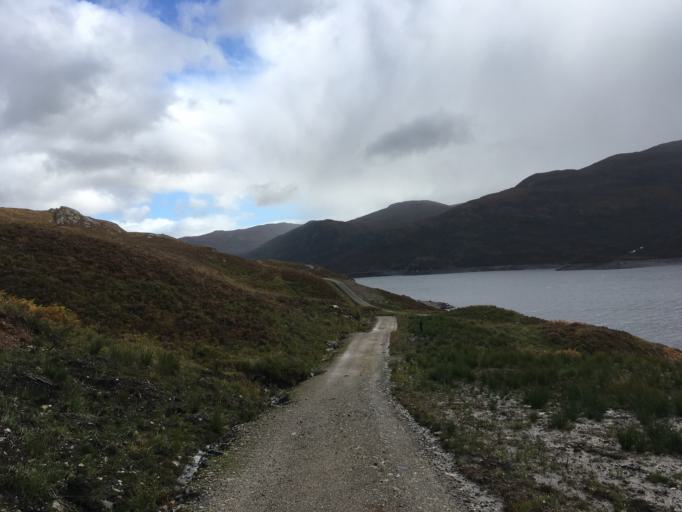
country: GB
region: Scotland
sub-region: Highland
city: Spean Bridge
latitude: 57.3418
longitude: -4.9802
